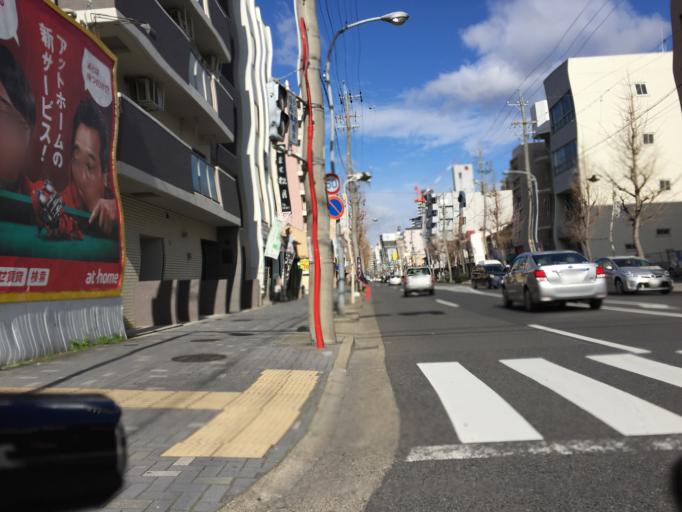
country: JP
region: Aichi
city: Nagoya-shi
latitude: 35.1659
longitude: 136.9253
